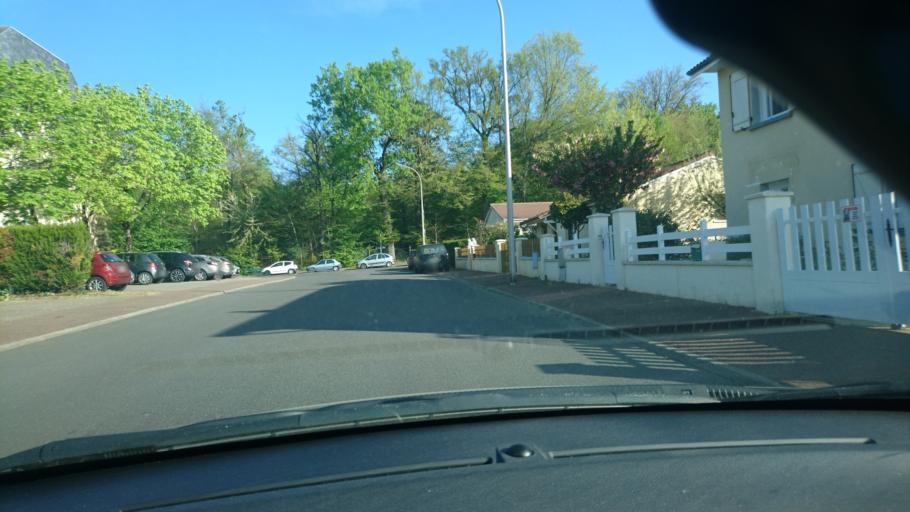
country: FR
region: Limousin
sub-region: Departement de la Haute-Vienne
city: Limoges
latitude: 45.8573
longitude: 1.2754
